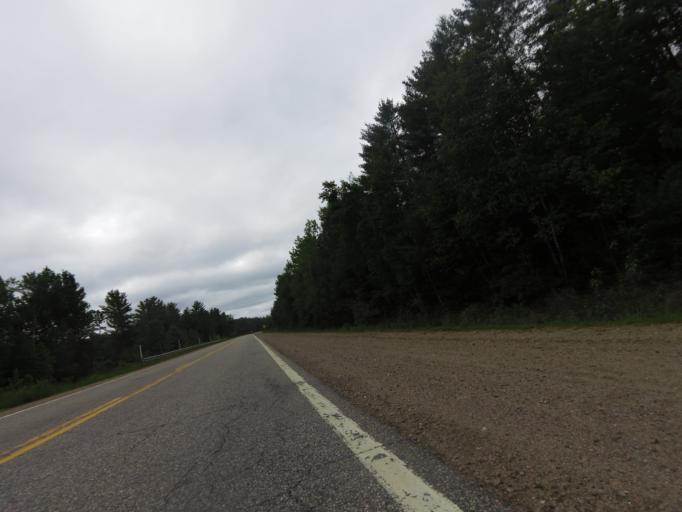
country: CA
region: Quebec
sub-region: Outaouais
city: Shawville
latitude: 45.8660
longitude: -76.4068
